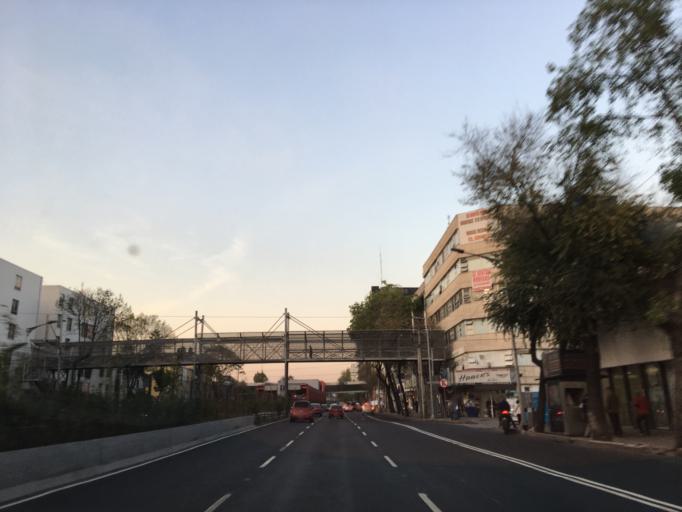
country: MX
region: Mexico City
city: Mexico City
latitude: 19.4142
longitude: -99.1348
